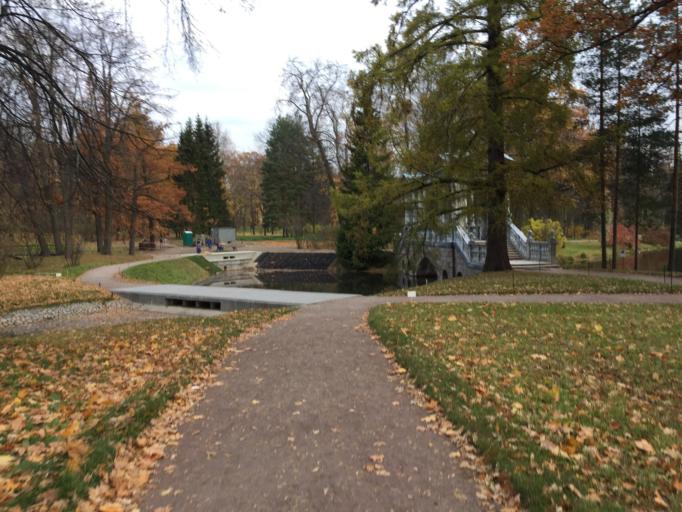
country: RU
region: St.-Petersburg
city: Pushkin
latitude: 59.7099
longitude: 30.3889
